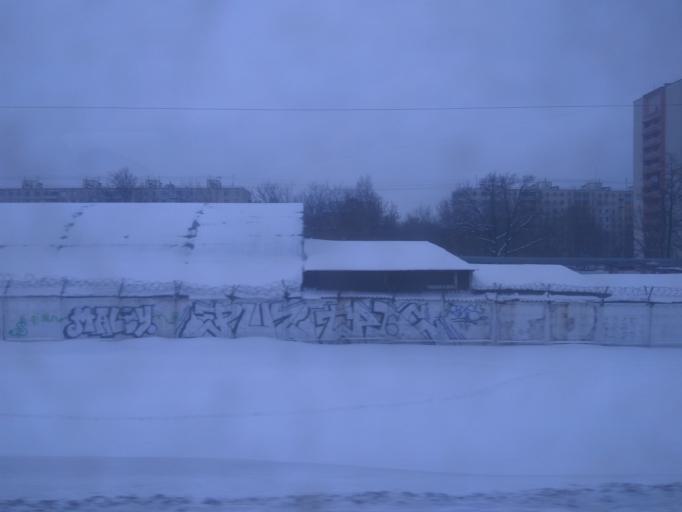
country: RU
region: Moscow
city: Lyublino
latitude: 55.6789
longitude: 37.7310
